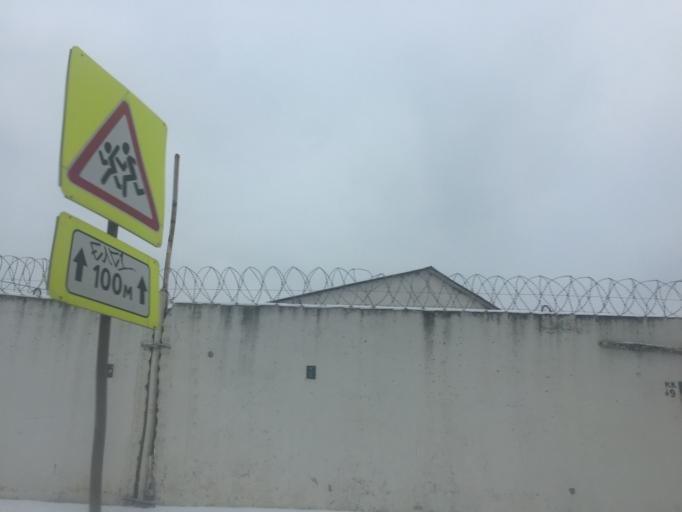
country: RU
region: Tula
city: Tula
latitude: 54.1712
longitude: 37.6287
